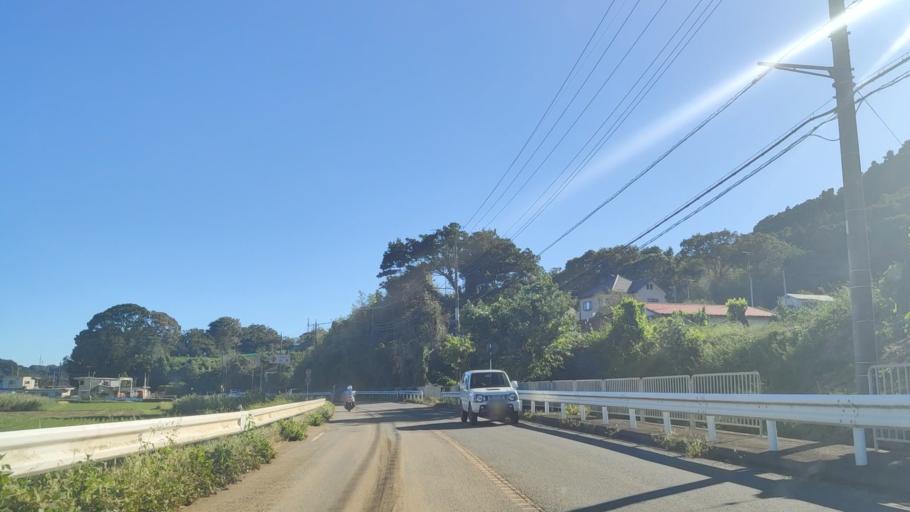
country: JP
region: Kanagawa
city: Zama
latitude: 35.5555
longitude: 139.3193
